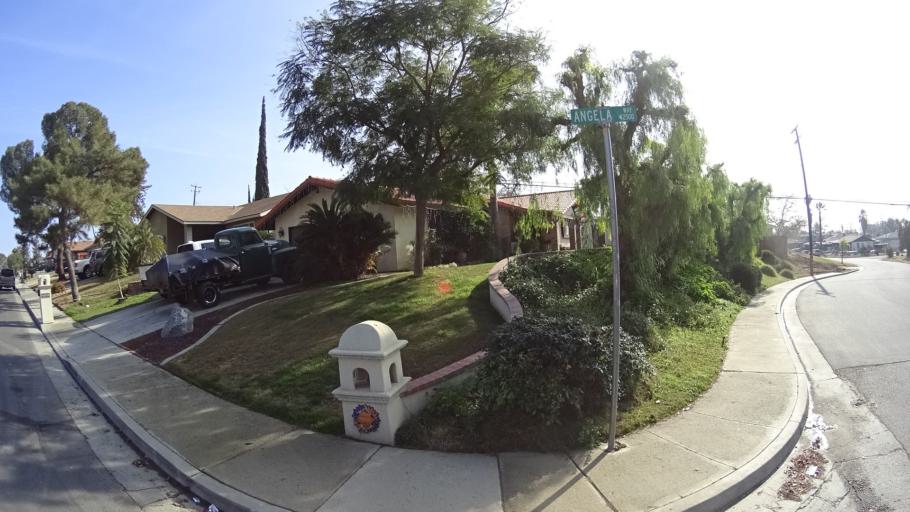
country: US
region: California
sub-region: Kern County
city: Bakersfield
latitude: 35.3871
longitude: -118.9623
